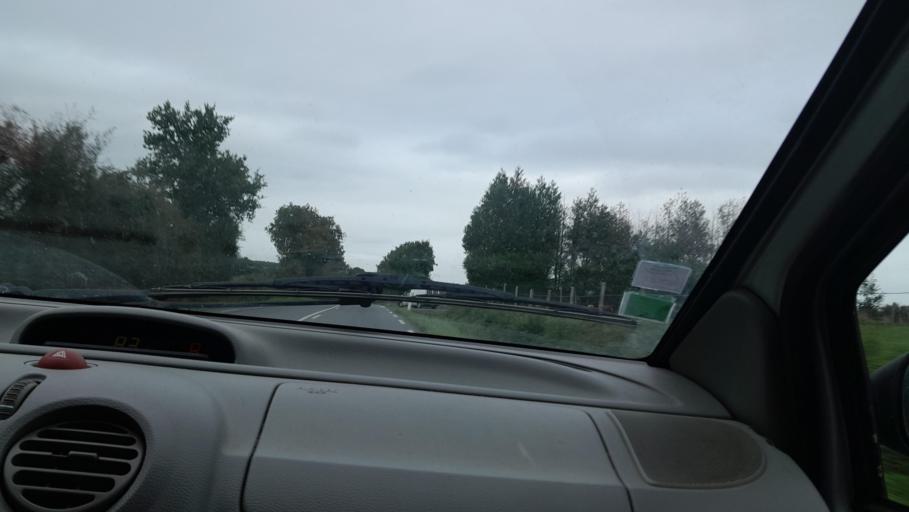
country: FR
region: Pays de la Loire
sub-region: Departement de Maine-et-Loire
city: Pouance
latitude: 47.6550
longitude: -1.1986
